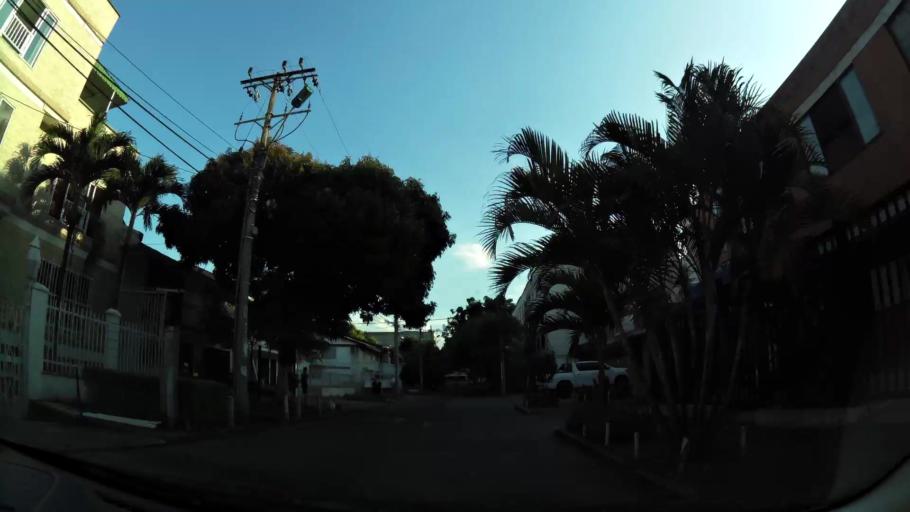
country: CO
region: Valle del Cauca
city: Cali
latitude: 3.3990
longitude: -76.5506
